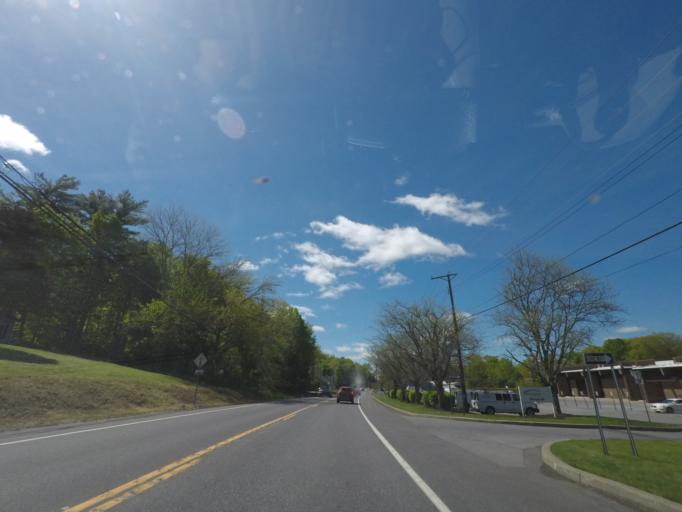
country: US
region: New York
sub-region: Ulster County
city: Lake Katrine
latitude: 41.9932
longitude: -73.9862
